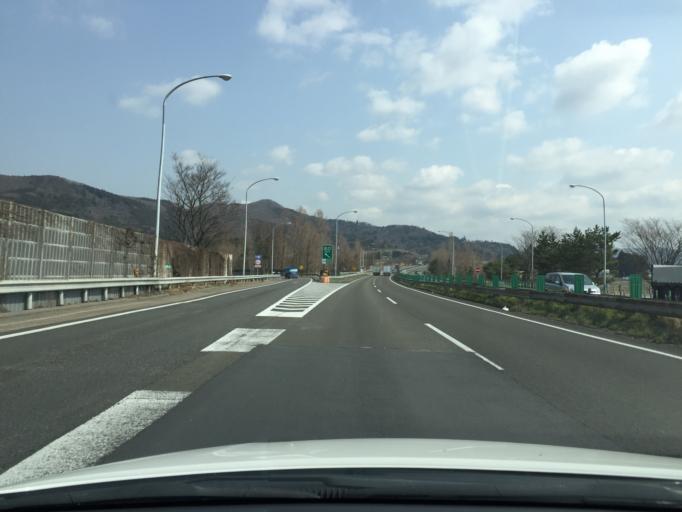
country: JP
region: Miyagi
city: Shiroishi
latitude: 38.0367
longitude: 140.6295
